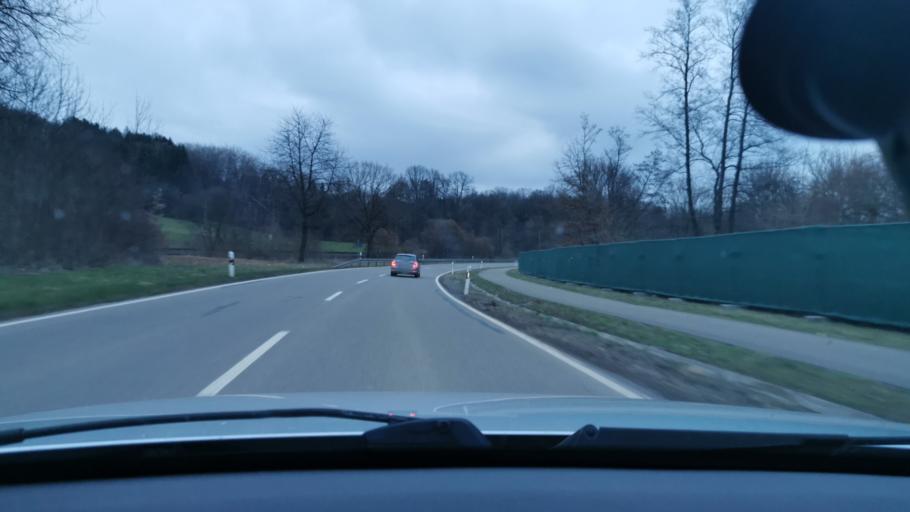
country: DE
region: Baden-Wuerttemberg
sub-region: Regierungsbezirk Stuttgart
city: Reichenbach an der Fils
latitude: 48.7123
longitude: 9.4901
